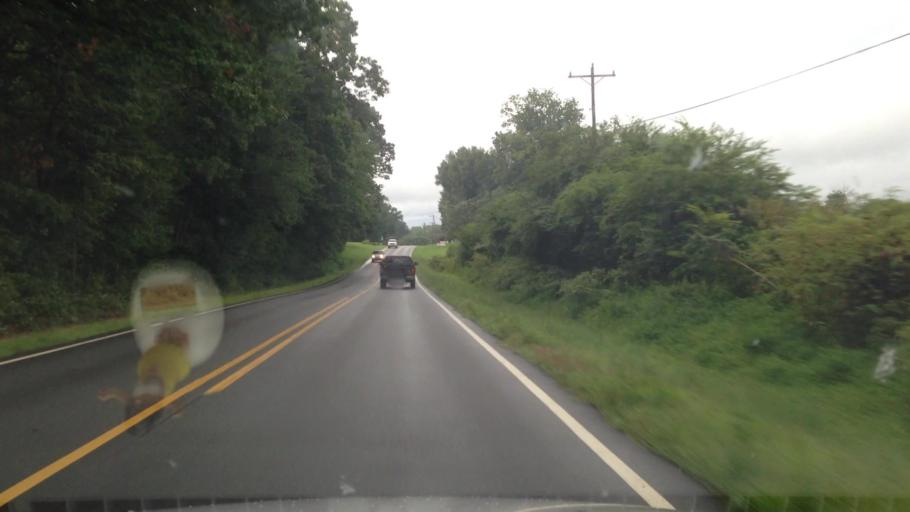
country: US
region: North Carolina
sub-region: Rockingham County
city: Reidsville
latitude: 36.2865
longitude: -79.7360
